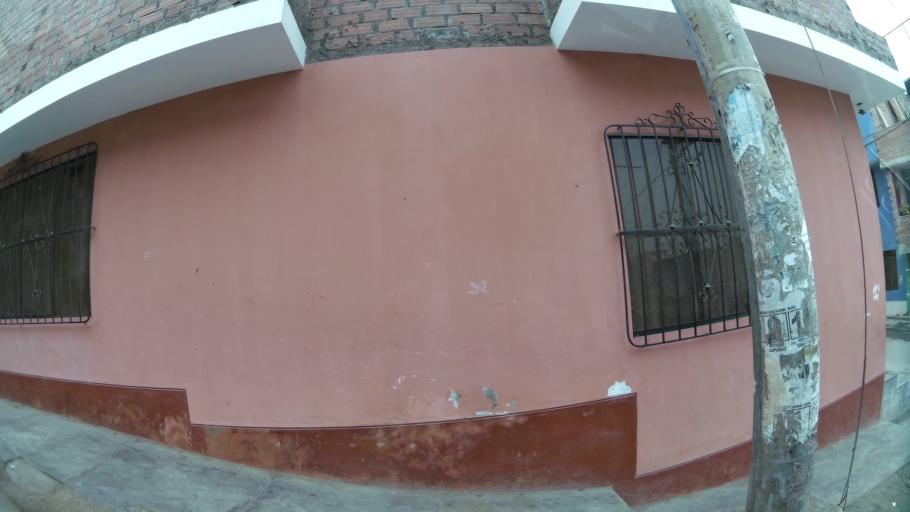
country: PE
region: Lima
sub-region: Lima
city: Surco
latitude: -12.1758
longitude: -76.9689
